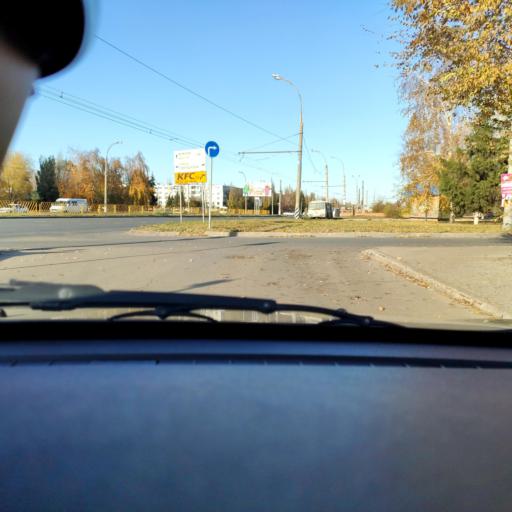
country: RU
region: Samara
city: Tol'yatti
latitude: 53.5256
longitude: 49.2970
